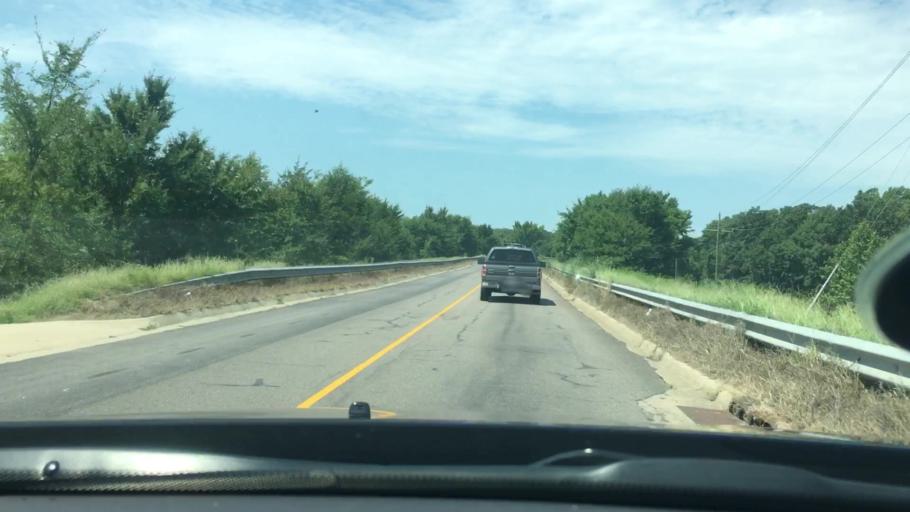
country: US
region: Oklahoma
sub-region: Pontotoc County
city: Ada
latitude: 34.7907
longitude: -96.6396
